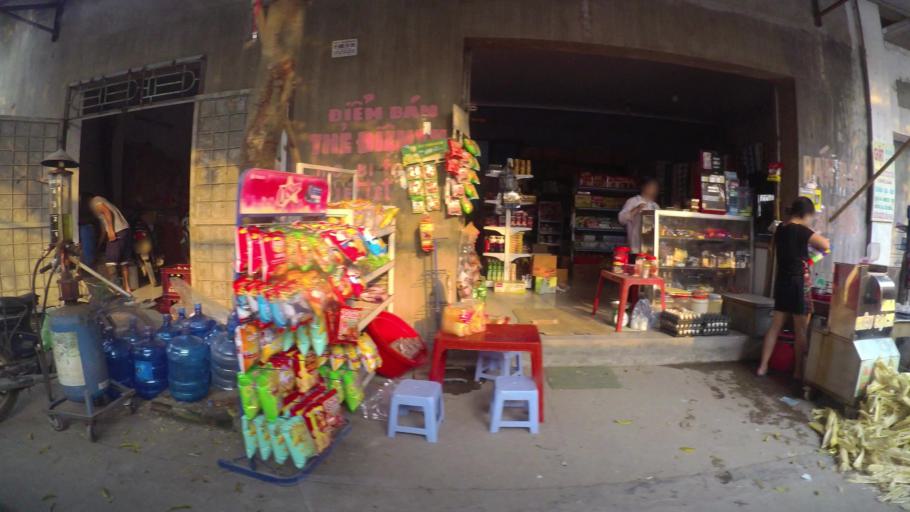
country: VN
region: Ha Noi
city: Cau Dien
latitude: 21.0057
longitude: 105.7248
